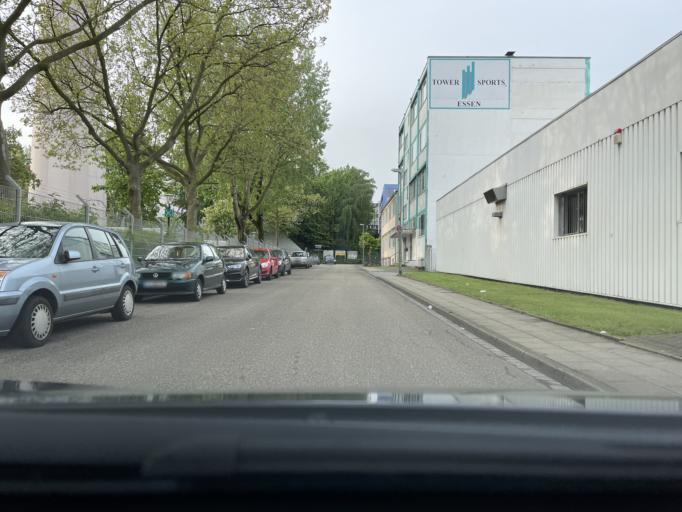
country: DE
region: North Rhine-Westphalia
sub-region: Regierungsbezirk Dusseldorf
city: Essen
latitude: 51.4481
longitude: 6.9959
